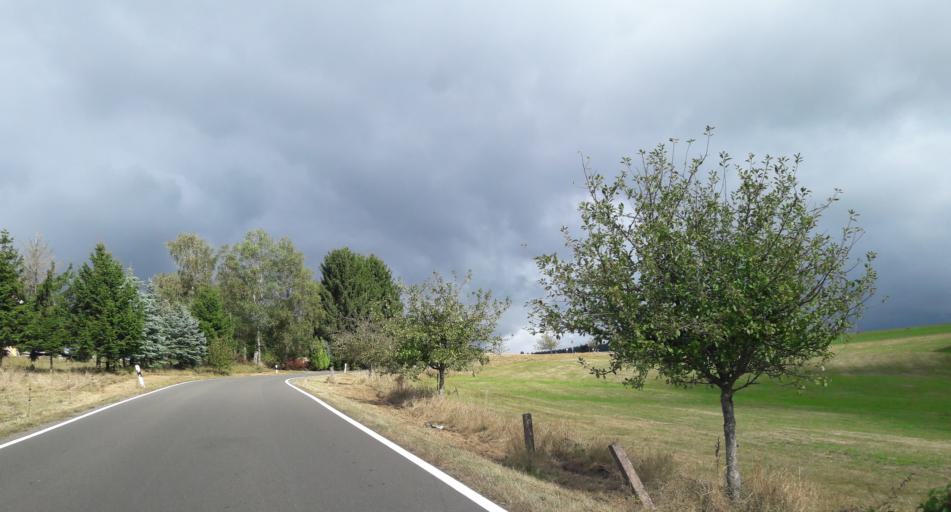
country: DE
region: Rheinland-Pfalz
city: Hahnweiler
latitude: 49.5245
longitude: 7.2115
